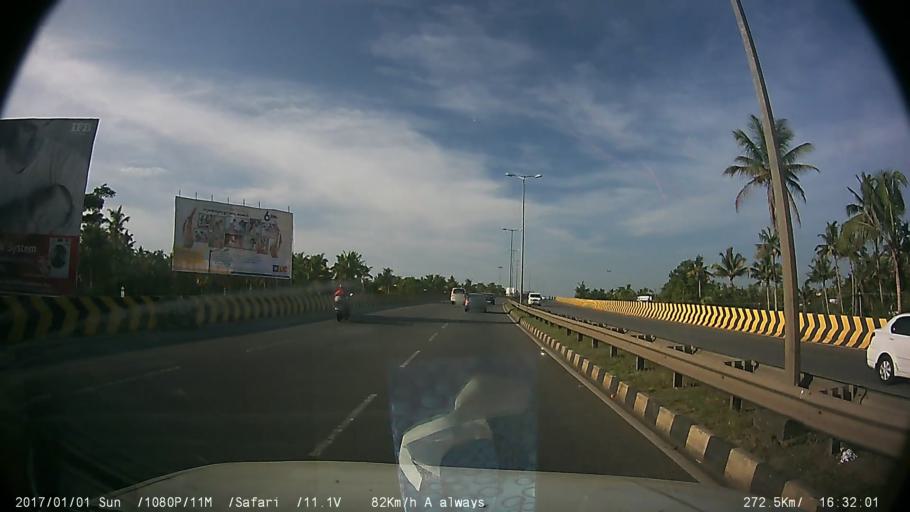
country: IN
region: Kerala
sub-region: Thrissur District
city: Kizhake Chalakudi
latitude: 10.3260
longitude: 76.3235
